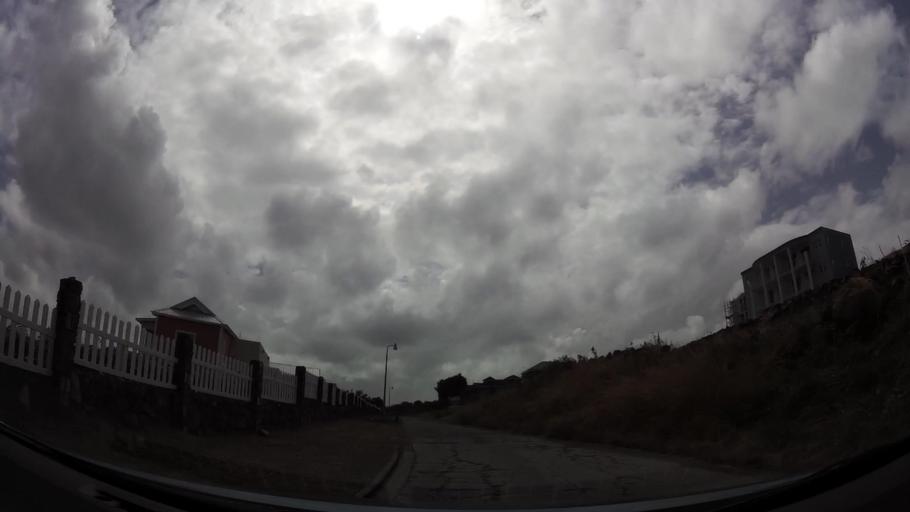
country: KN
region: Saint Peter Basseterre
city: Monkey Hill
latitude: 17.2988
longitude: -62.6910
